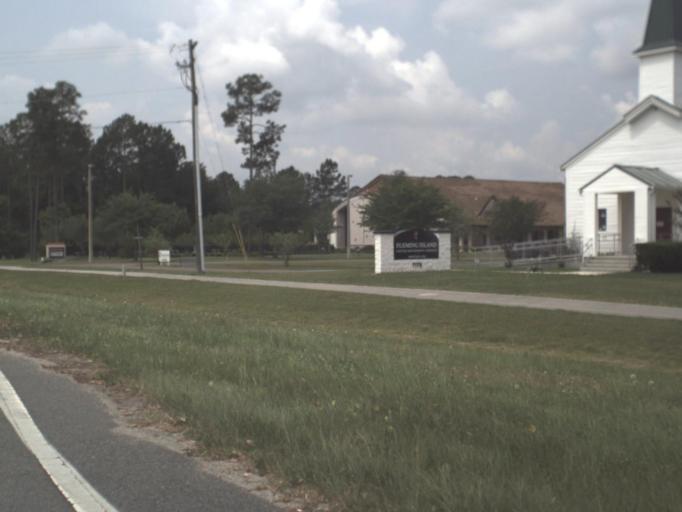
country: US
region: Florida
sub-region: Clay County
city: Green Cove Springs
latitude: 30.0636
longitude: -81.7077
